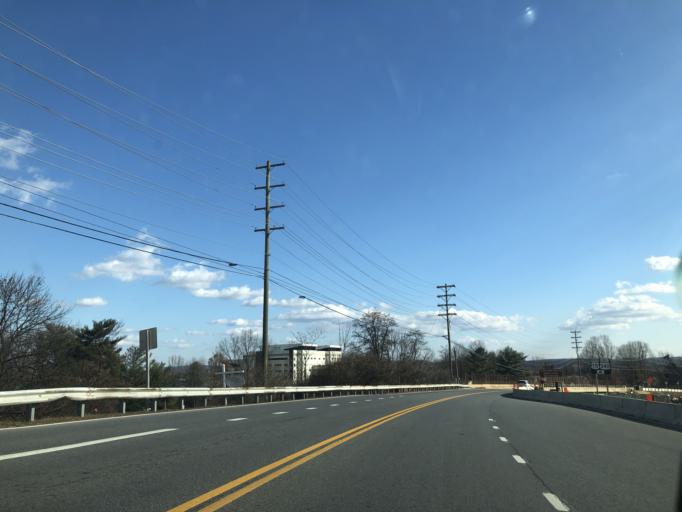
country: US
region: Maryland
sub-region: Frederick County
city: Ballenger Creek
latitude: 39.4029
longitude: -77.4395
